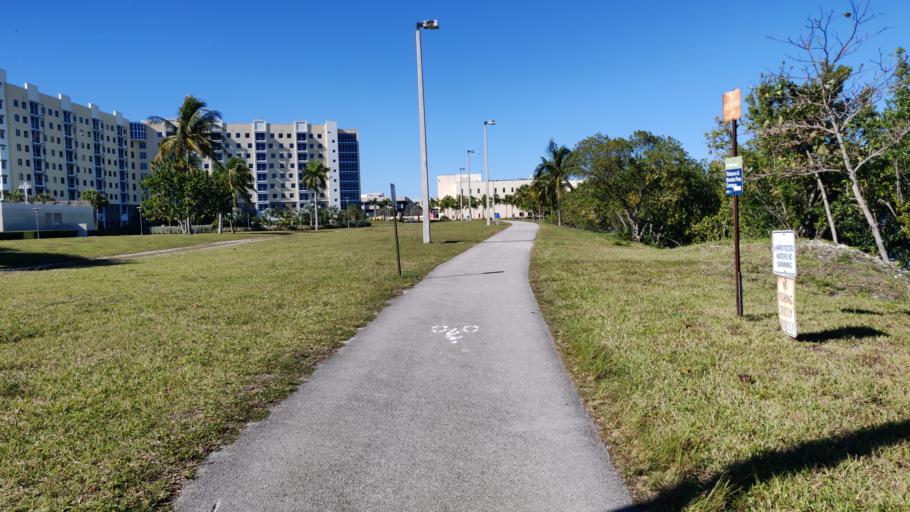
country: US
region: Florida
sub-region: Miami-Dade County
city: Bal Harbour
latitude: 25.9068
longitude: -80.1375
